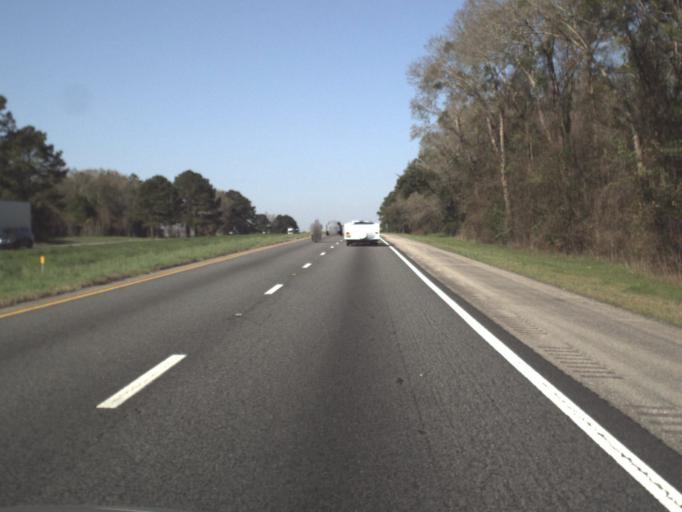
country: US
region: Florida
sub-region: Leon County
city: Tallahassee
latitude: 30.4783
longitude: -84.1097
